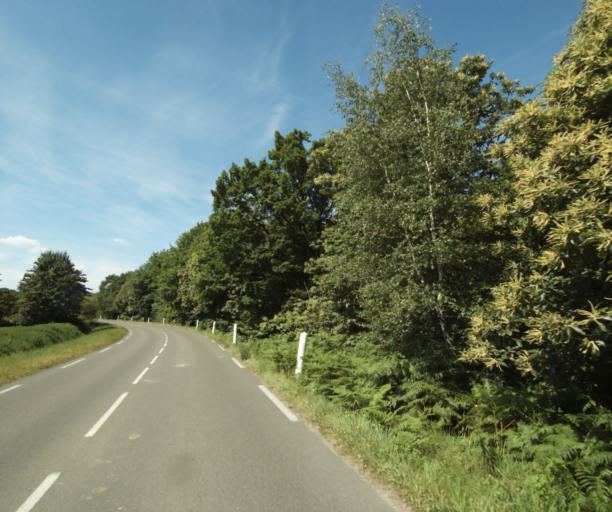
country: FR
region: Pays de la Loire
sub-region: Departement de la Mayenne
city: Laval
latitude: 48.0427
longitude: -0.7777
